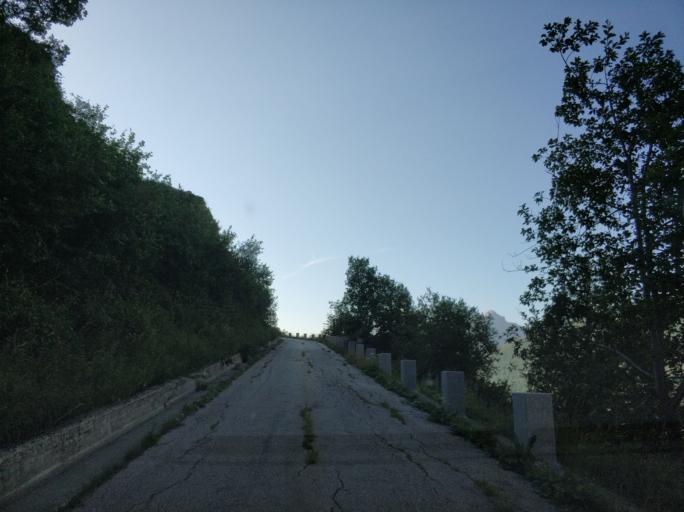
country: IT
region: Piedmont
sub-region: Provincia di Torino
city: Usseglio
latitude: 45.2499
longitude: 7.1779
